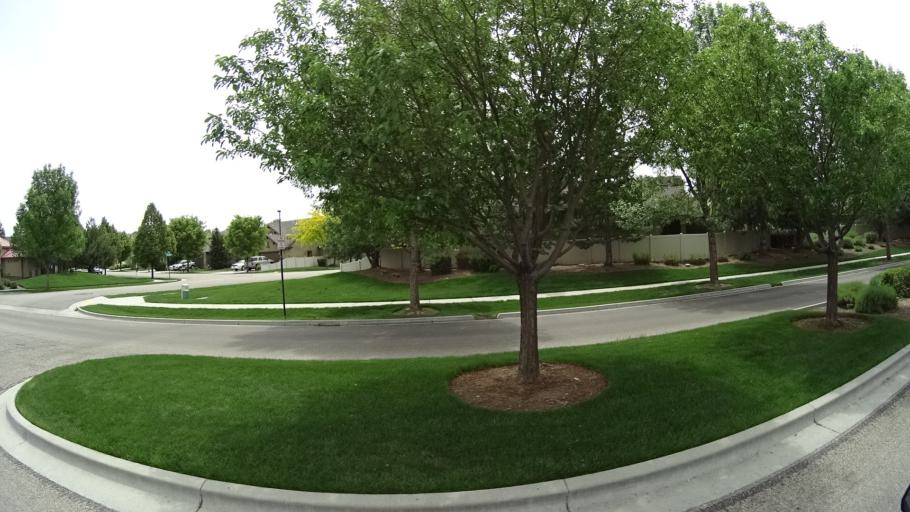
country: US
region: Idaho
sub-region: Ada County
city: Meridian
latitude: 43.5664
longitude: -116.3583
